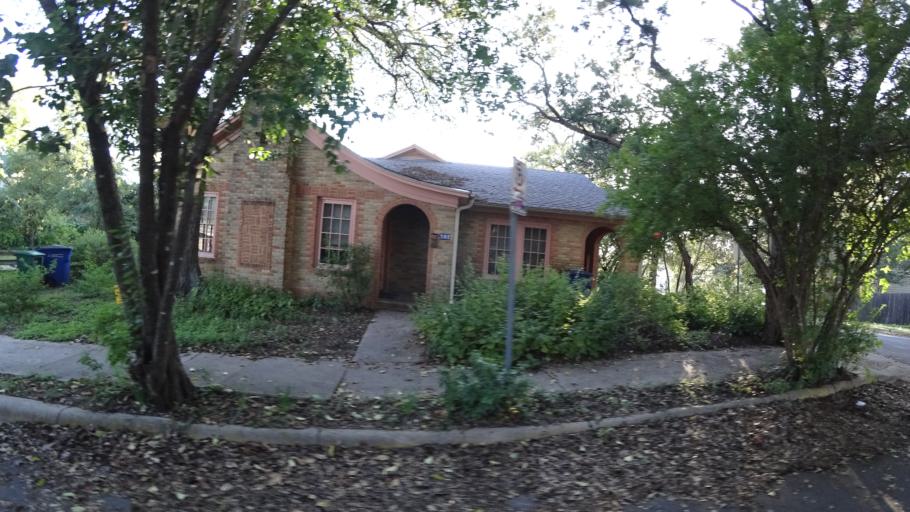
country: US
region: Texas
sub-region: Travis County
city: Austin
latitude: 30.2950
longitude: -97.7351
